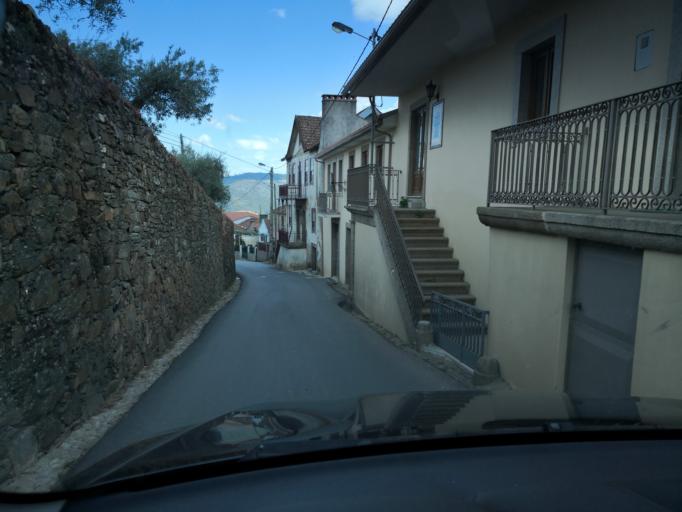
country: PT
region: Vila Real
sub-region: Sabrosa
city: Vilela
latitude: 41.2104
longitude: -7.6640
